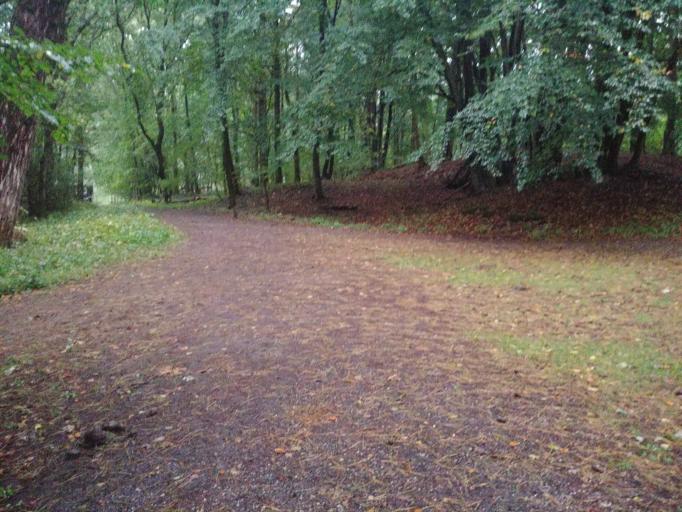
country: NL
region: North Holland
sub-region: Gemeente Heemstede
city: Heemstede
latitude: 52.3750
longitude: 4.5875
